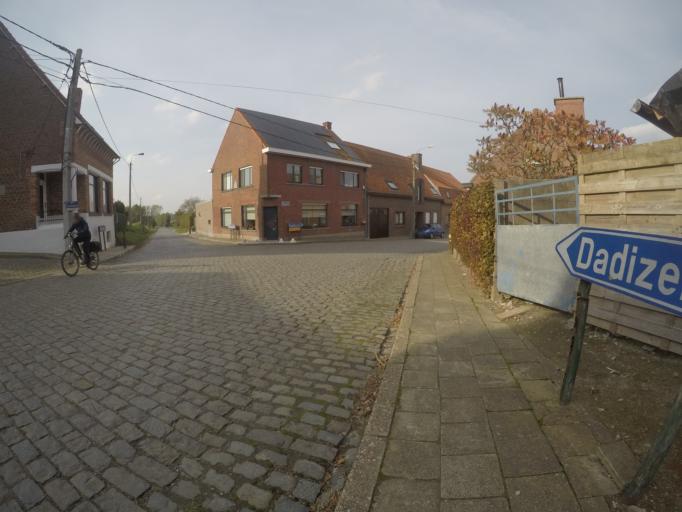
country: BE
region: Flanders
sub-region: Provincie West-Vlaanderen
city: Moorslede
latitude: 50.8426
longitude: 3.0591
